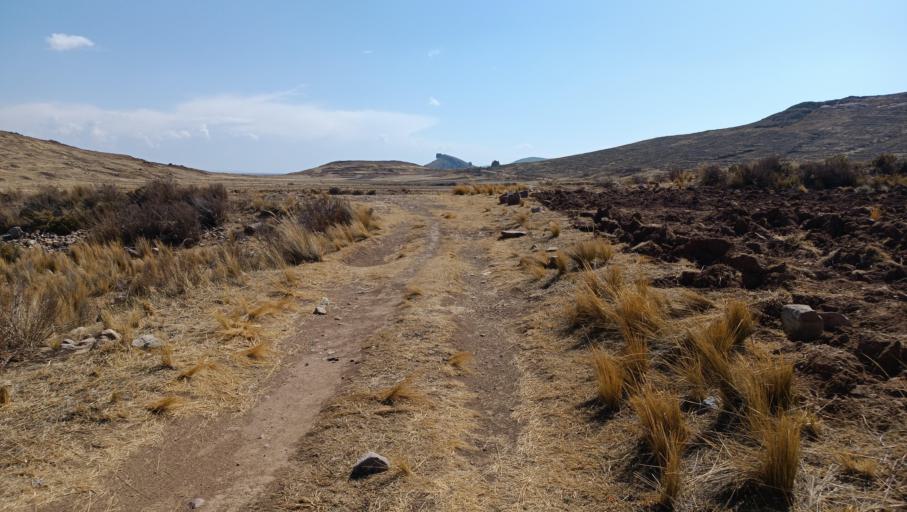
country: BO
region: La Paz
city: Batallas
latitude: -16.3484
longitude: -68.6658
